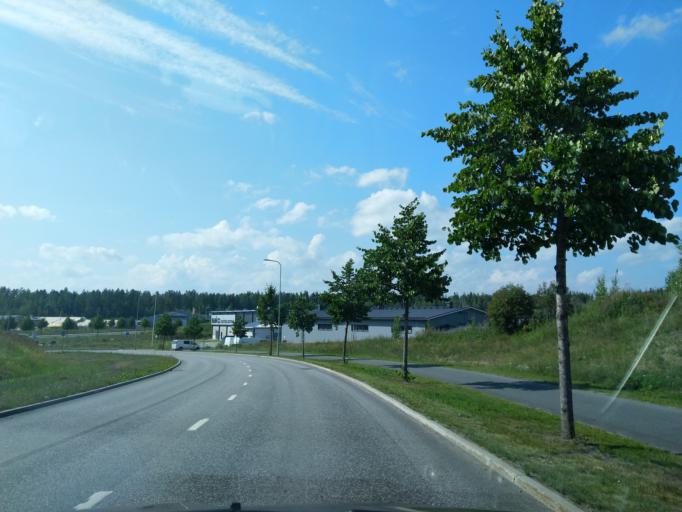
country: FI
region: South Karelia
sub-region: Lappeenranta
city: Lappeenranta
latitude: 61.0393
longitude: 28.1157
